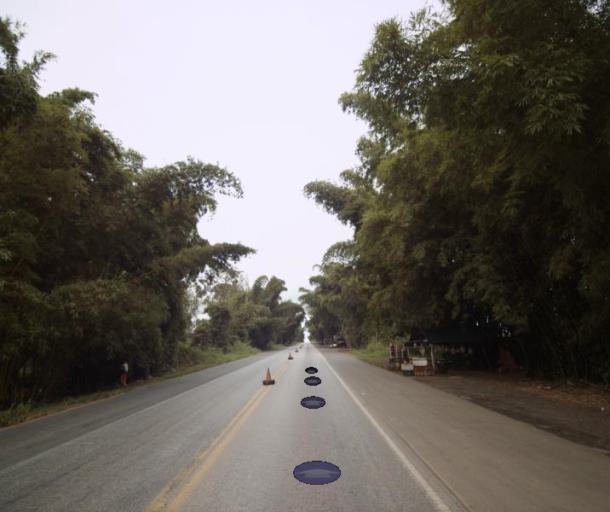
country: BR
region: Goias
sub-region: Uruacu
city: Uruacu
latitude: -14.6241
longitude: -49.1723
